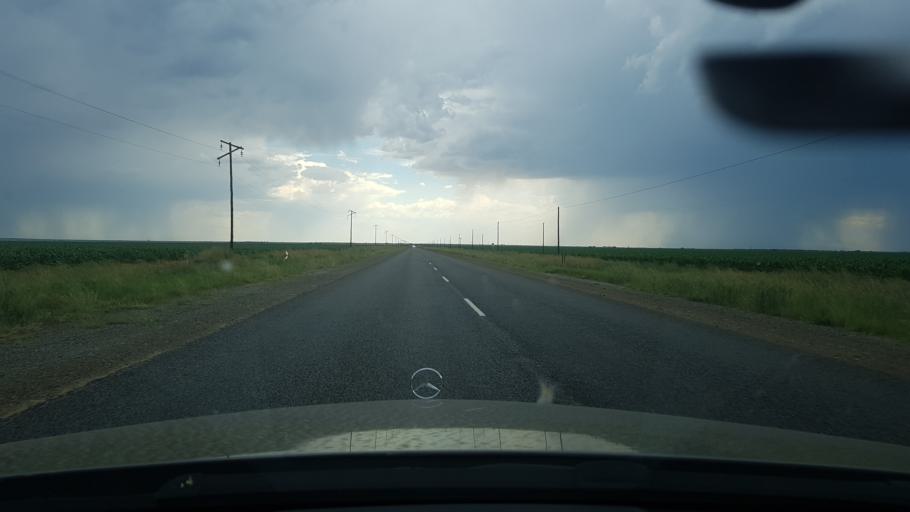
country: ZA
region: Orange Free State
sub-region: Lejweleputswa District Municipality
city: Hoopstad
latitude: -28.0059
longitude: 25.6266
